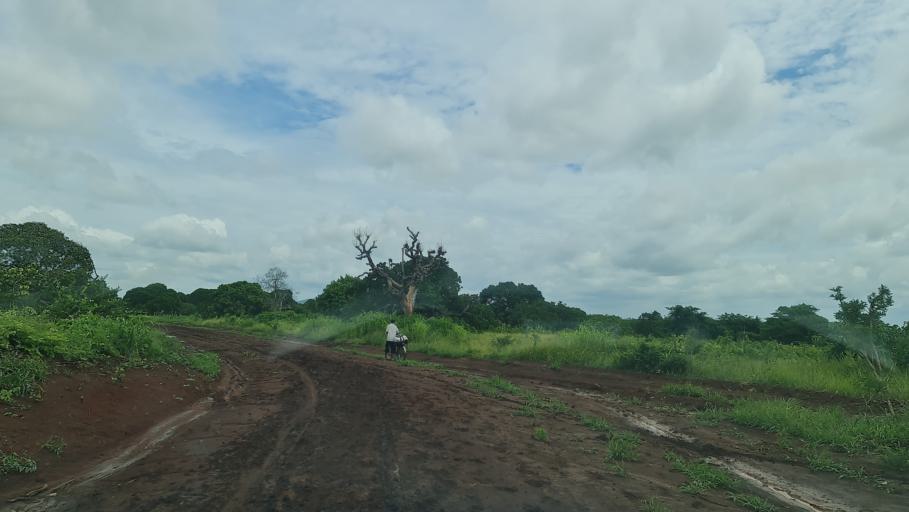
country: MZ
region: Cabo Delgado
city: Pemba
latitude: -13.5436
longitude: 40.0222
